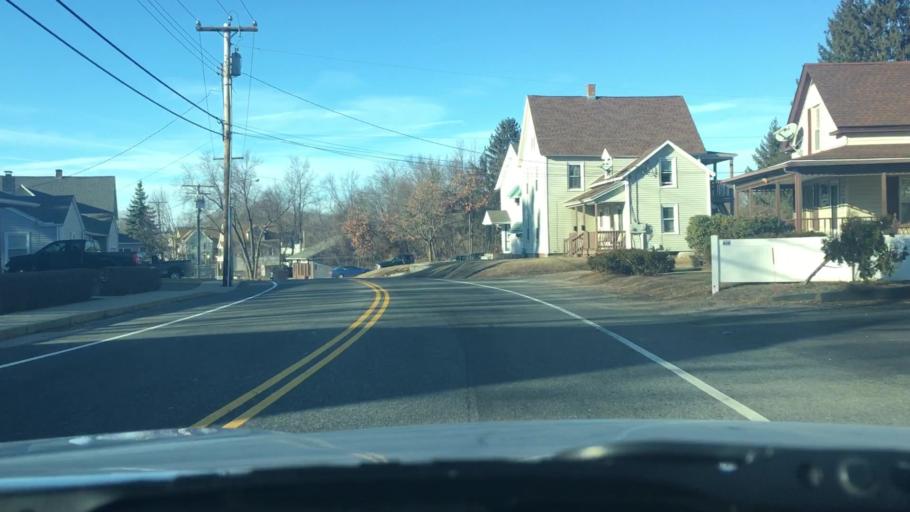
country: US
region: Massachusetts
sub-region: Hampden County
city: Ludlow
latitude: 42.1639
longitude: -72.4840
